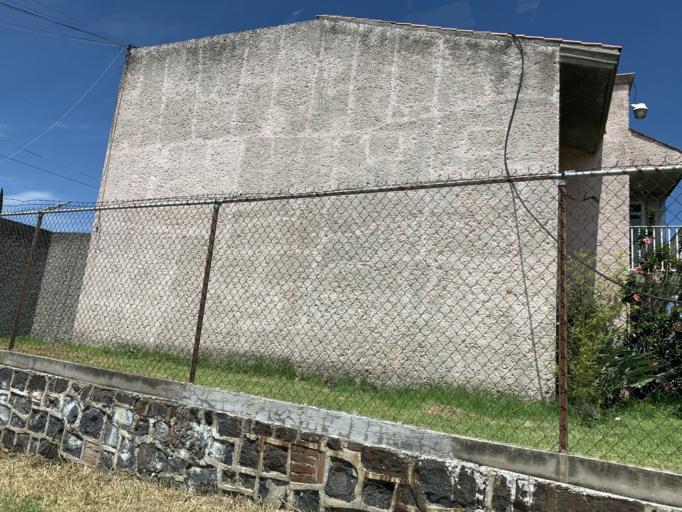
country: MX
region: Puebla
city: Cuautlancingo
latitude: 19.0810
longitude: -98.2755
